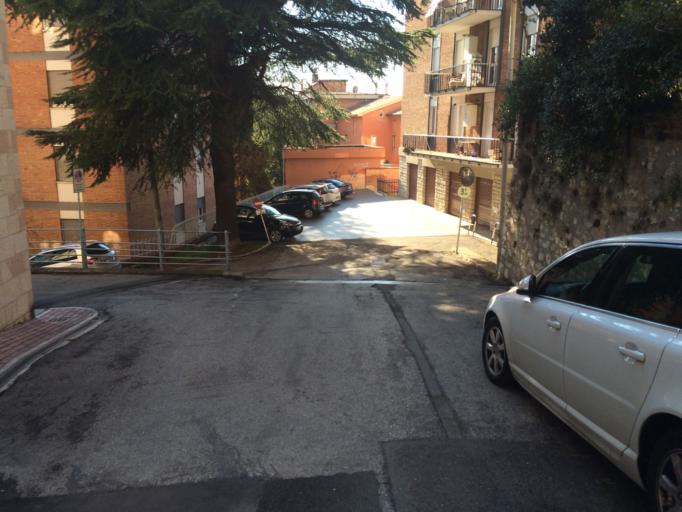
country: IT
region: Umbria
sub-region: Provincia di Perugia
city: Perugia
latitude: 43.1019
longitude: 12.3875
